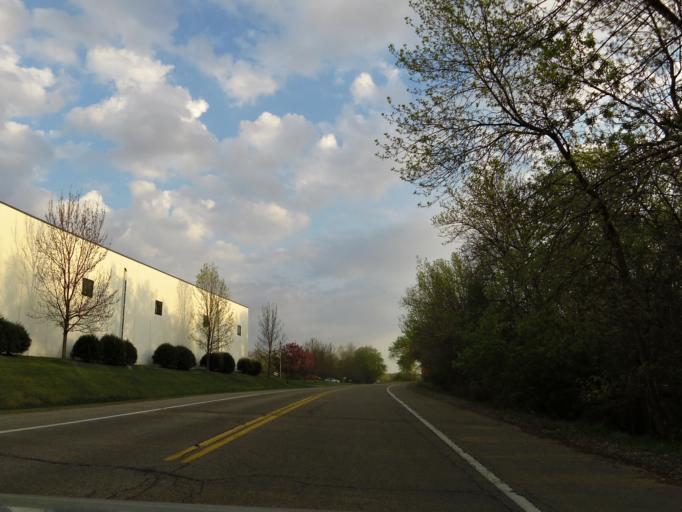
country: US
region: Minnesota
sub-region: Dakota County
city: Mendota Heights
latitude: 44.8690
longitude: -93.1725
